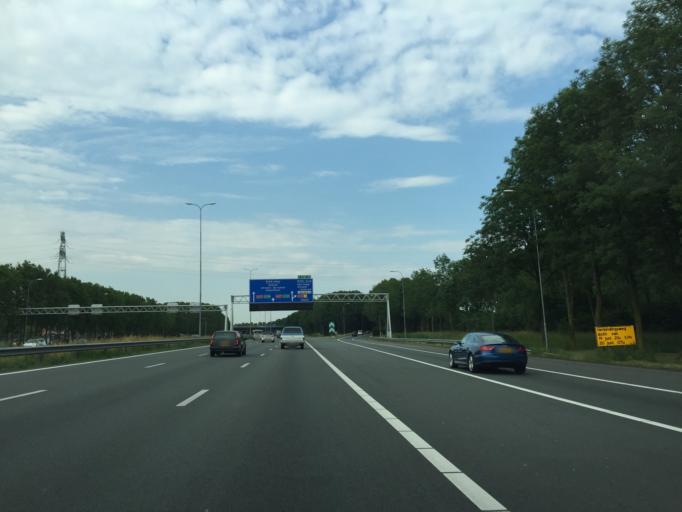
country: NL
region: Utrecht
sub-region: Gemeente Utrecht
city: Lunetten
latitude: 52.0486
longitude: 5.1428
